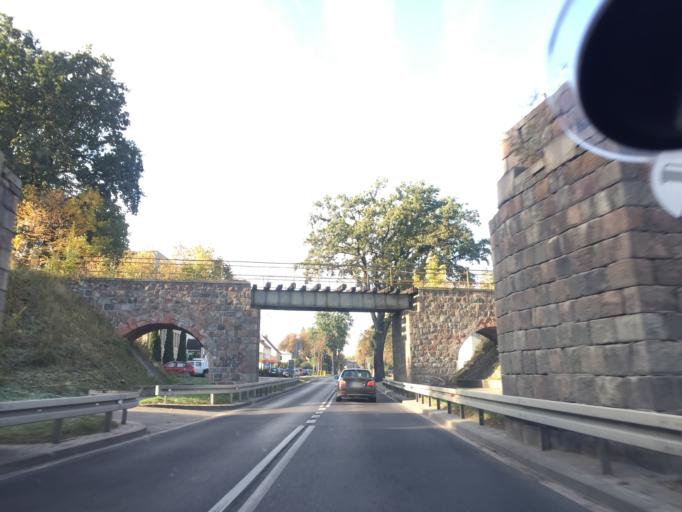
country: PL
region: Warmian-Masurian Voivodeship
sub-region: Powiat lidzbarski
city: Lidzbark Warminski
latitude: 54.1270
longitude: 20.5959
